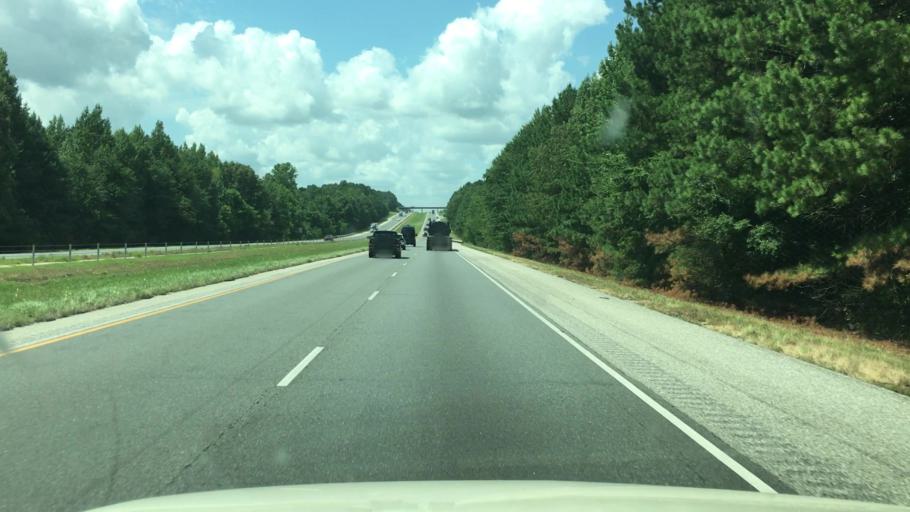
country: US
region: Arkansas
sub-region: Clark County
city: Arkadelphia
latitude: 34.0825
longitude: -93.1146
